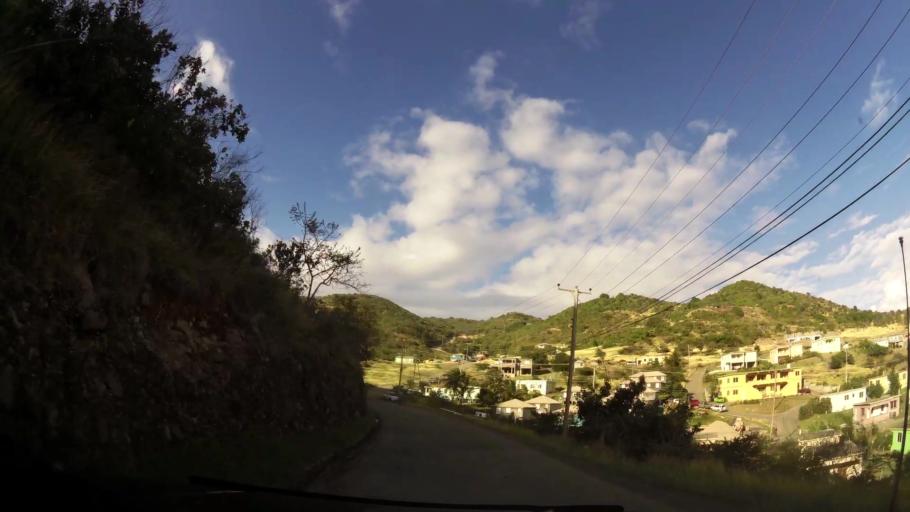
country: MS
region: Saint Peter
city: Brades
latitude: 16.7982
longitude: -62.1946
